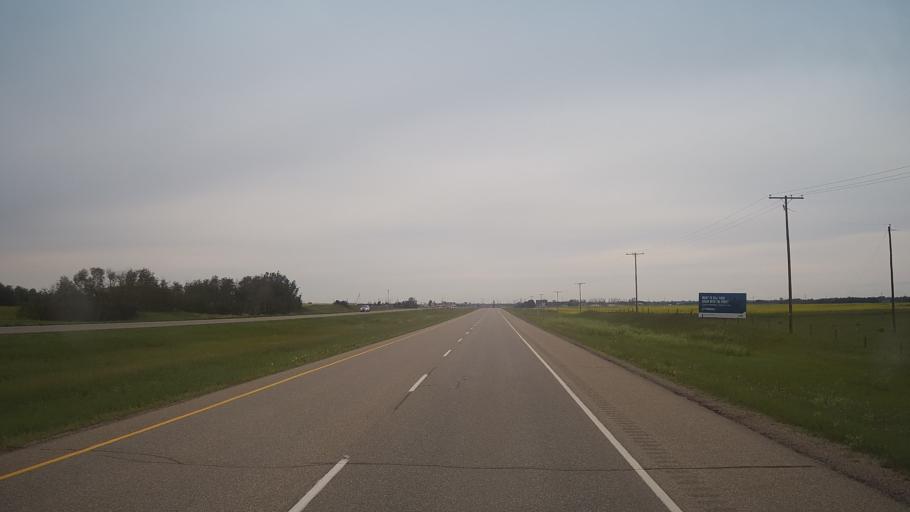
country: CA
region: Saskatchewan
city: Saskatoon
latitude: 52.0408
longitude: -106.5895
